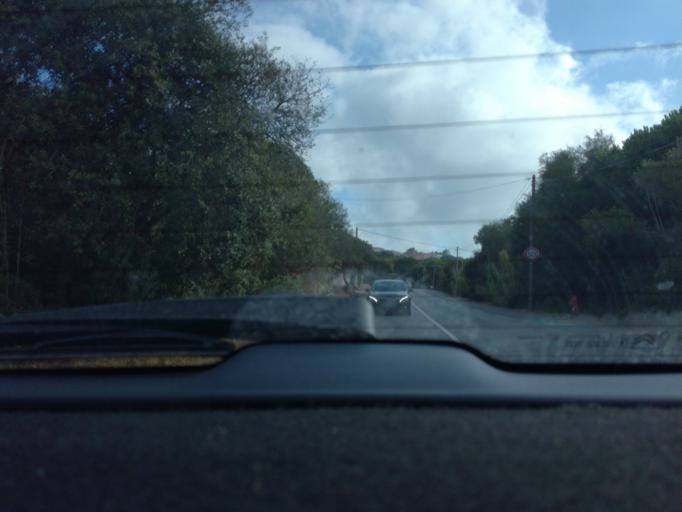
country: FR
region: Provence-Alpes-Cote d'Azur
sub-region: Departement du Var
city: Hyeres
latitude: 43.0441
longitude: 6.1349
